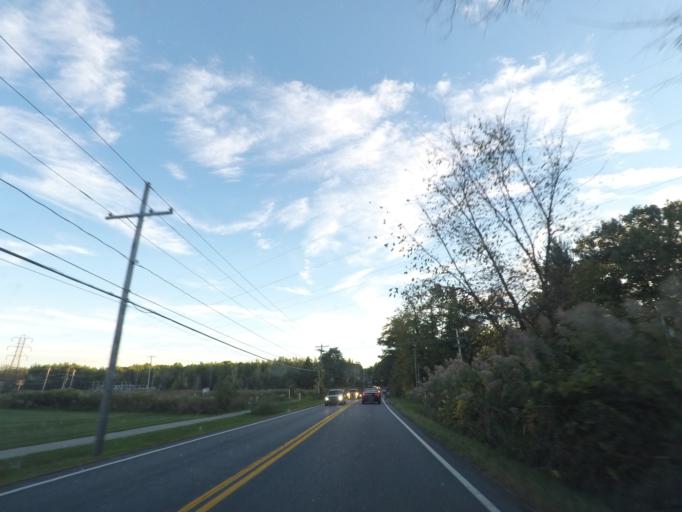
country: US
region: New York
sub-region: Albany County
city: Colonie
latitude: 42.7330
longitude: -73.8264
